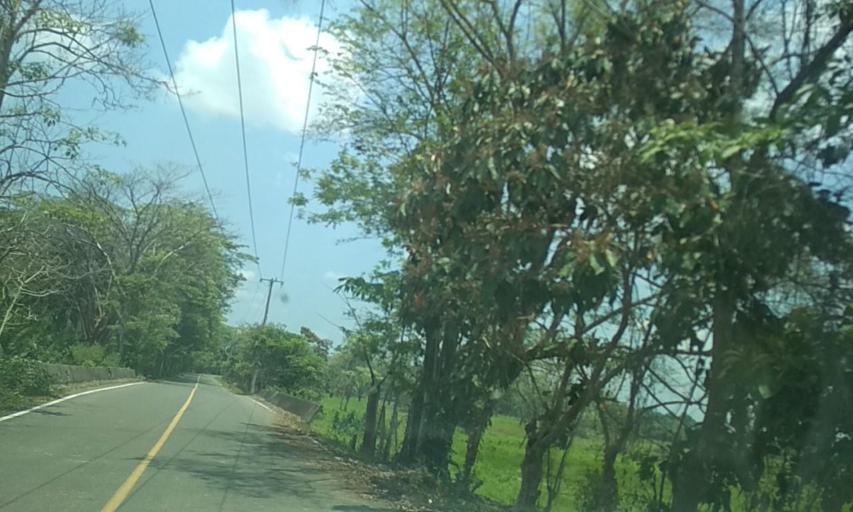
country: MX
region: Tabasco
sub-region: Huimanguillo
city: Francisco Rueda
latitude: 17.7519
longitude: -94.0299
